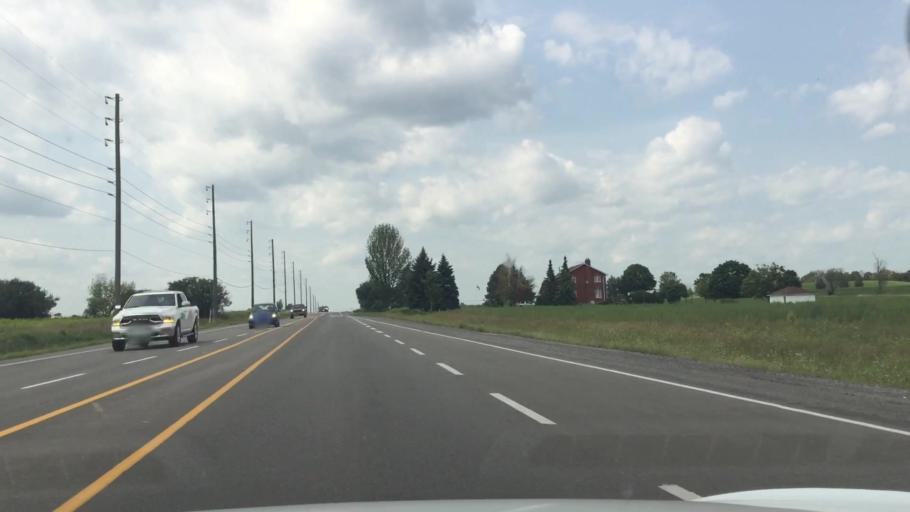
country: CA
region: Ontario
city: Oshawa
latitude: 43.9587
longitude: -78.8579
